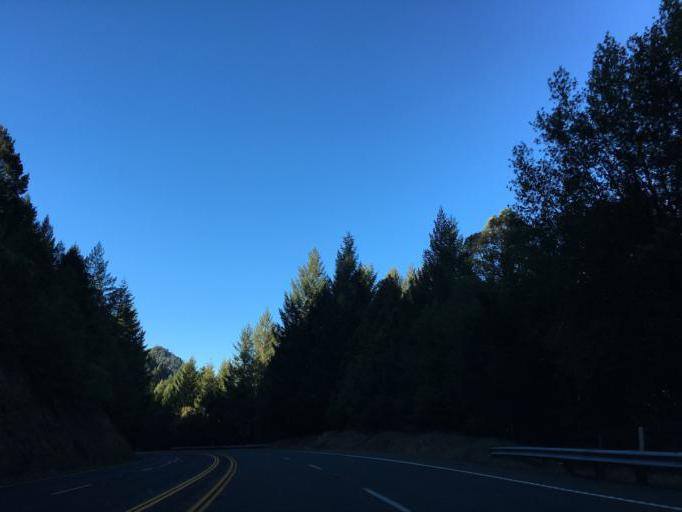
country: US
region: California
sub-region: Mendocino County
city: Brooktrails
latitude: 39.5407
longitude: -123.4183
